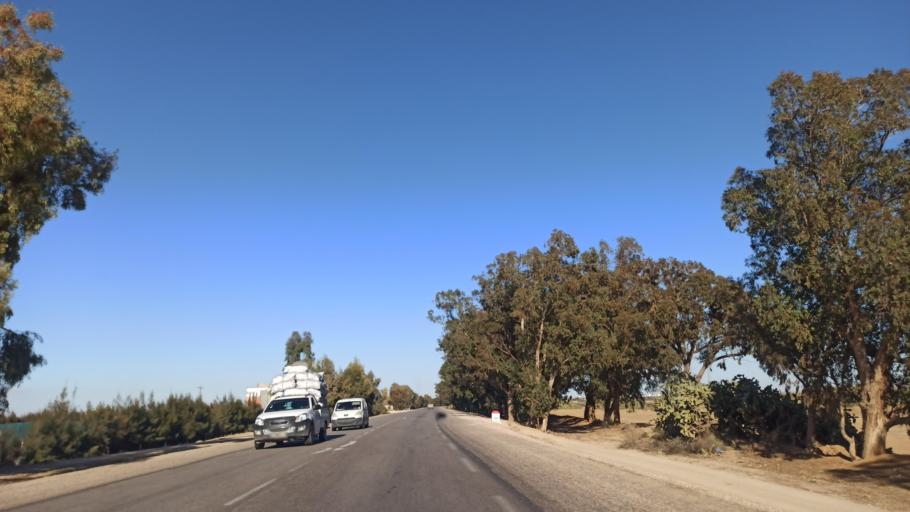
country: TN
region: Sidi Bu Zayd
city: Jilma
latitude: 35.2274
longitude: 9.3835
